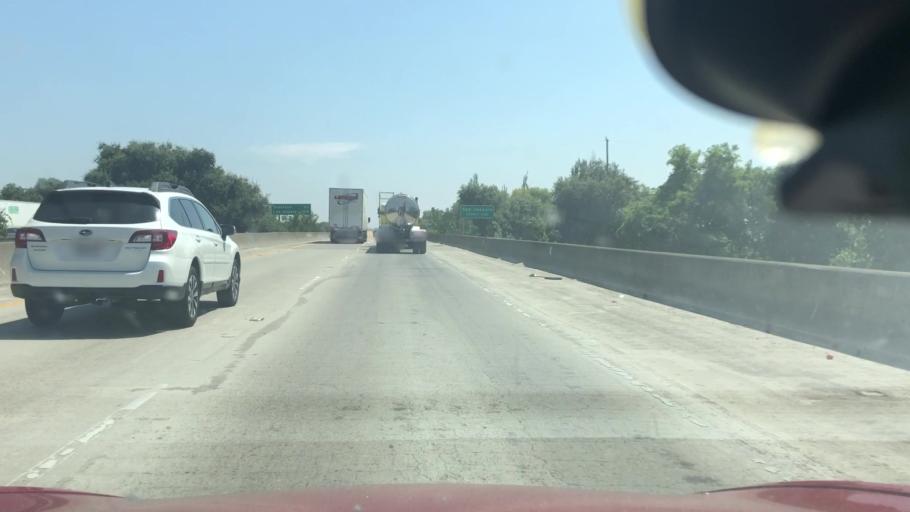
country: US
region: California
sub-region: San Joaquin County
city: Thornton
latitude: 38.2552
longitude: -121.4483
